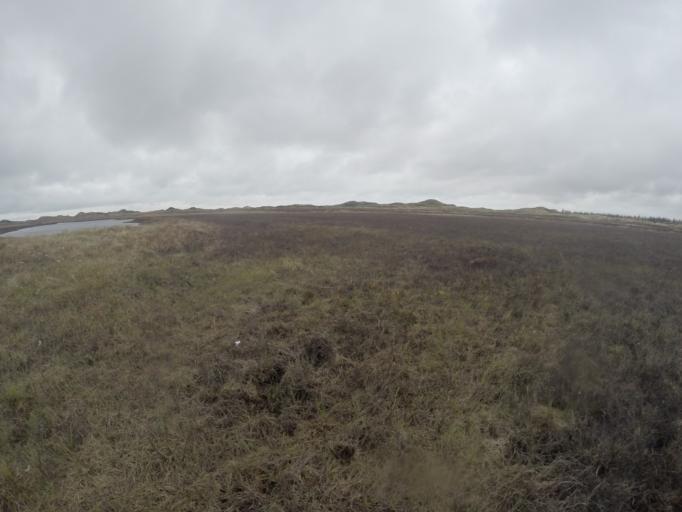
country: DK
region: North Denmark
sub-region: Thisted Kommune
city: Hurup
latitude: 56.8957
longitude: 8.3334
